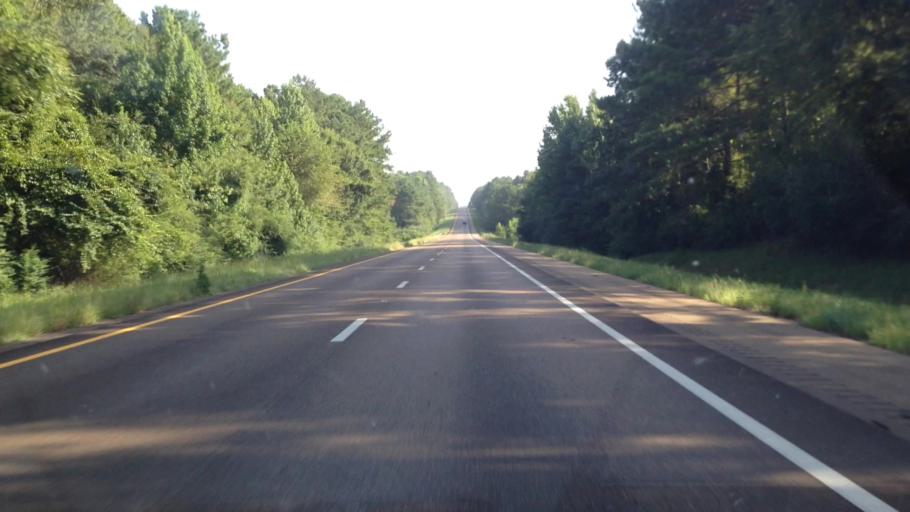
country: US
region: Mississippi
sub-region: Pike County
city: Summit
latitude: 31.3909
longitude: -90.4792
